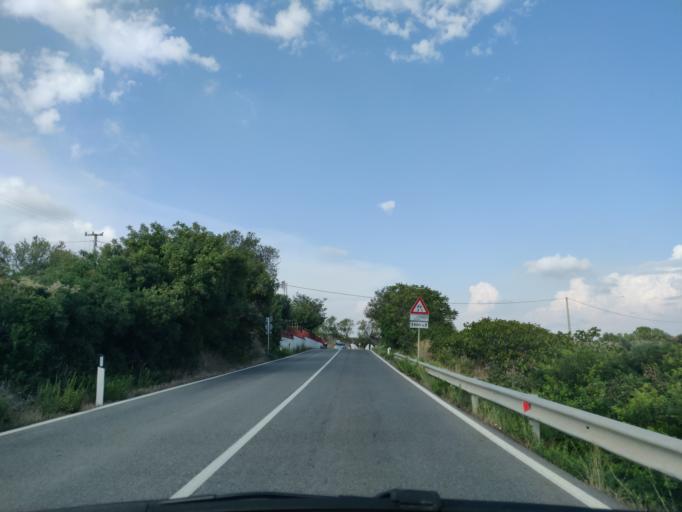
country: IT
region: Latium
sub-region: Provincia di Viterbo
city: Tarquinia
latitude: 42.2369
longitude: 11.7969
